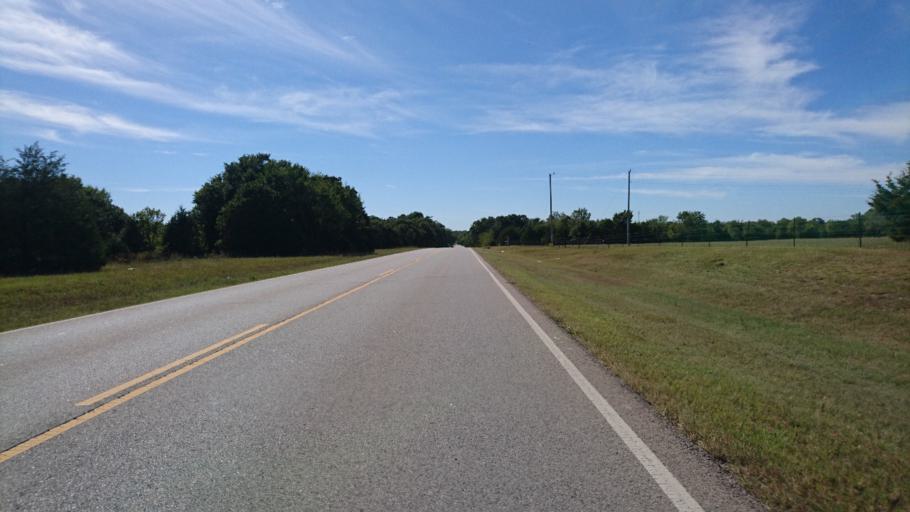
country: US
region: Oklahoma
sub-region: Lincoln County
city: Stroud
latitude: 35.7403
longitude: -96.7093
